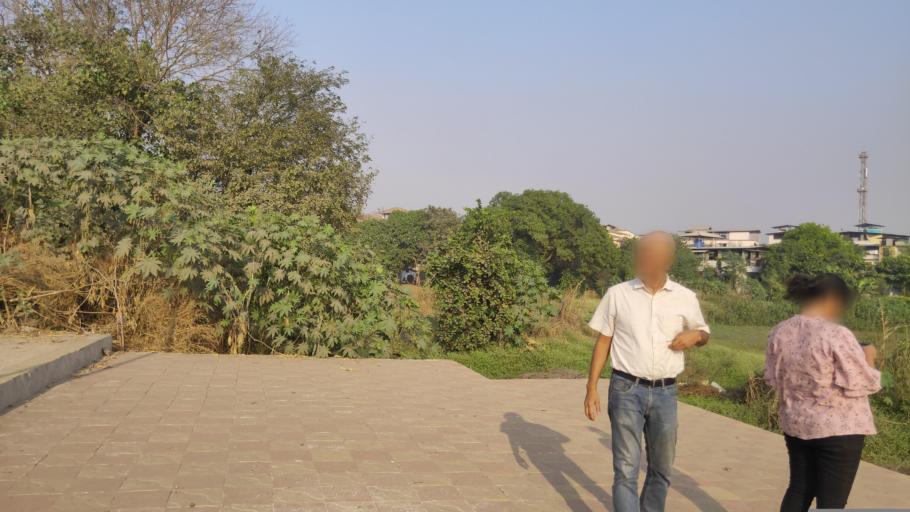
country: IN
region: Maharashtra
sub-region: Thane
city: Kalyan
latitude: 19.3147
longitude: 73.1575
